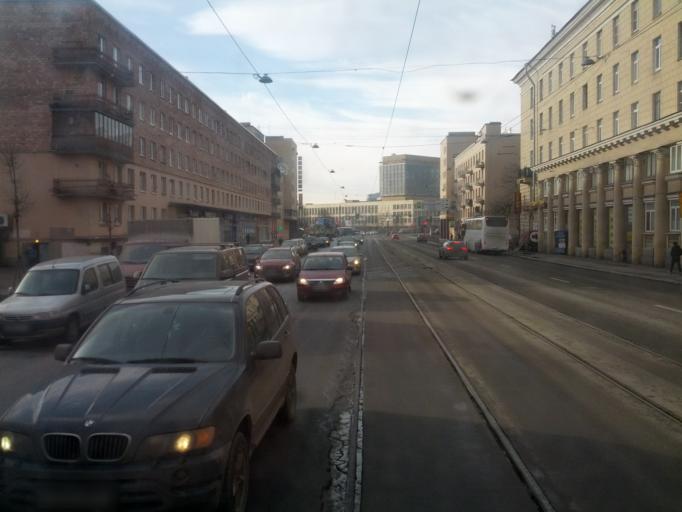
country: RU
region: Leningrad
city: Finlyandskiy
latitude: 59.9450
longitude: 30.4136
